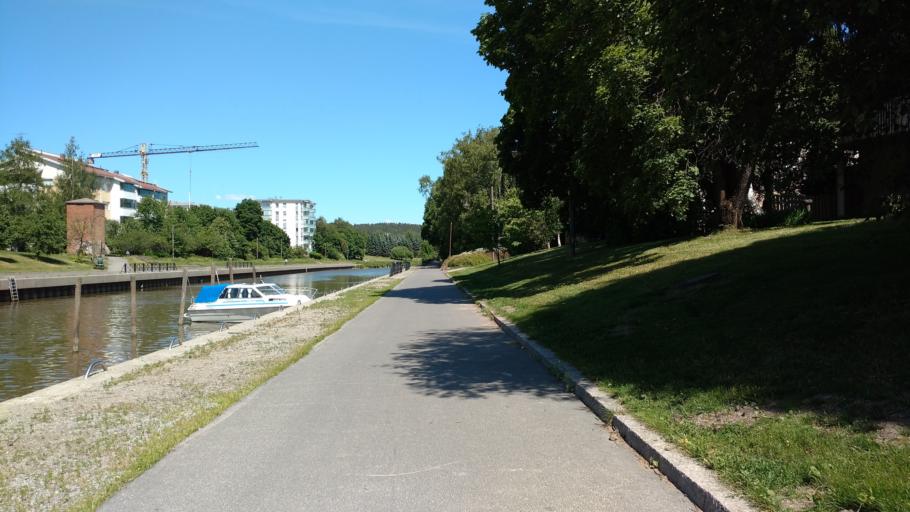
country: FI
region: Varsinais-Suomi
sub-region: Salo
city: Salo
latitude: 60.3881
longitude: 23.1293
